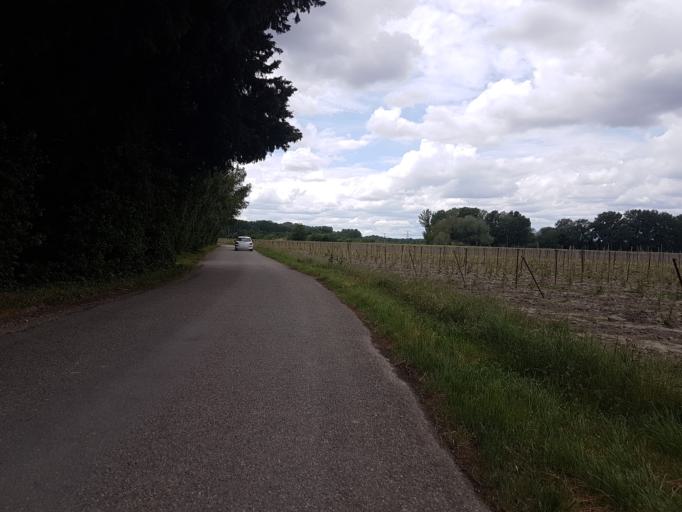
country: FR
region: Languedoc-Roussillon
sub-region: Departement du Gard
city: Vallabregues
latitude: 43.8702
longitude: 4.6224
